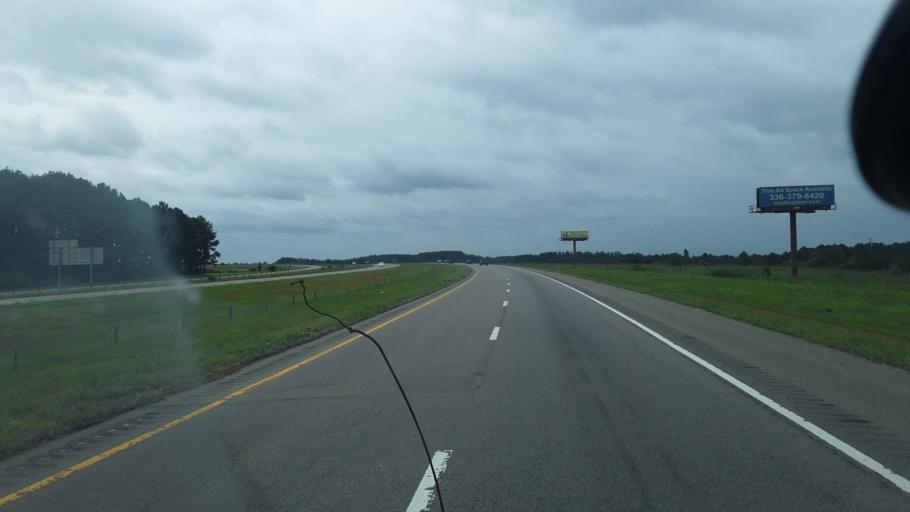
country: US
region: North Carolina
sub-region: Richmond County
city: Ellerbe
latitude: 35.1948
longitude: -79.7273
